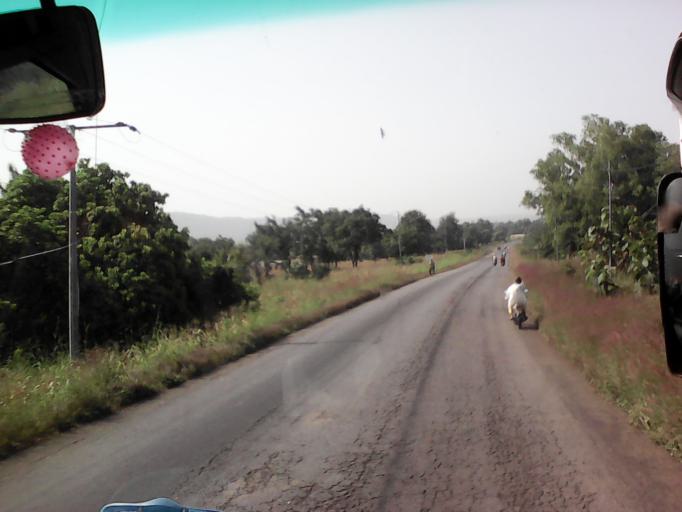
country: TG
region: Centrale
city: Sokode
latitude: 9.1080
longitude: 1.1440
